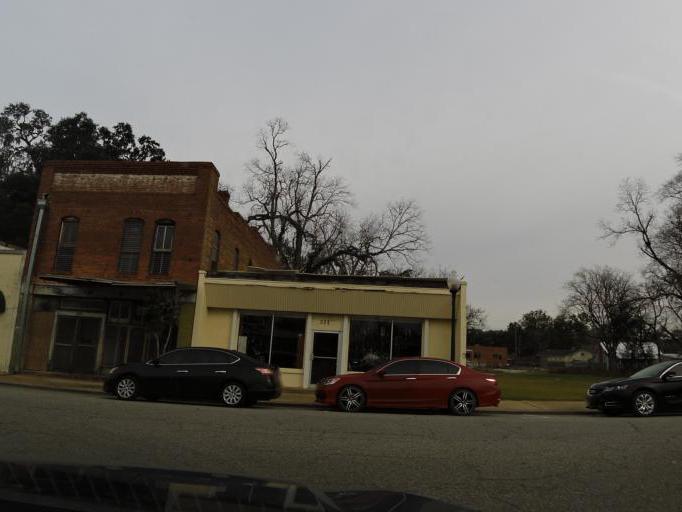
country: US
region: Georgia
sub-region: Decatur County
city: Bainbridge
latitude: 30.9079
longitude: -84.5757
